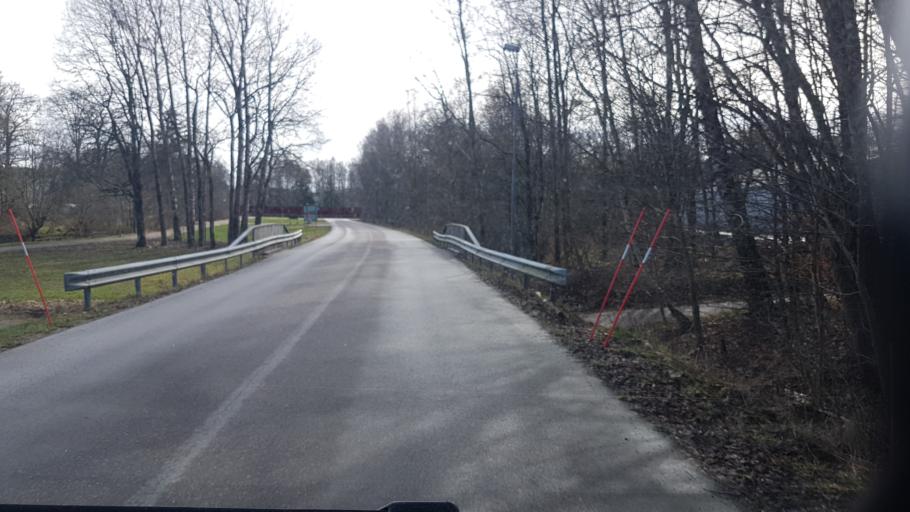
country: SE
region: Vaestra Goetaland
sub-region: Lerums Kommun
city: Stenkullen
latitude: 57.8071
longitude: 12.3739
